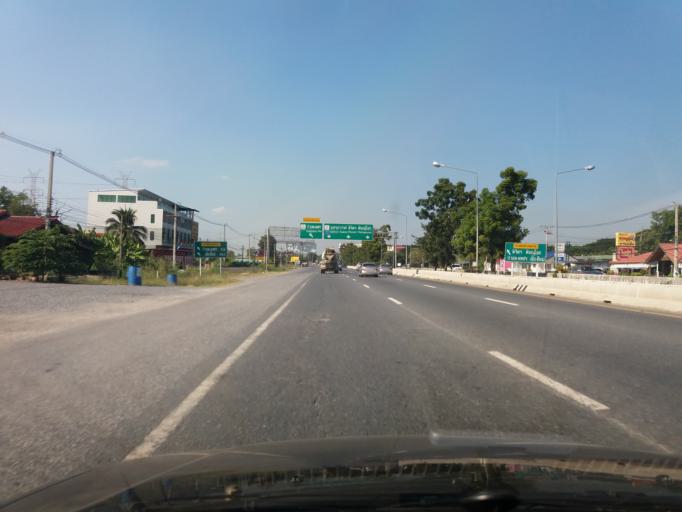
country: TH
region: Nakhon Sawan
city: Krok Phra
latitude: 15.6099
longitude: 100.1214
